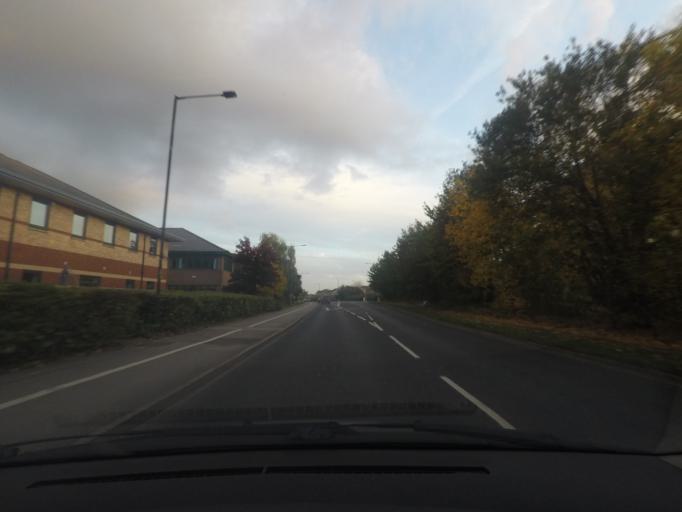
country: GB
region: England
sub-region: City of York
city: Skelton
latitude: 53.9884
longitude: -1.1044
